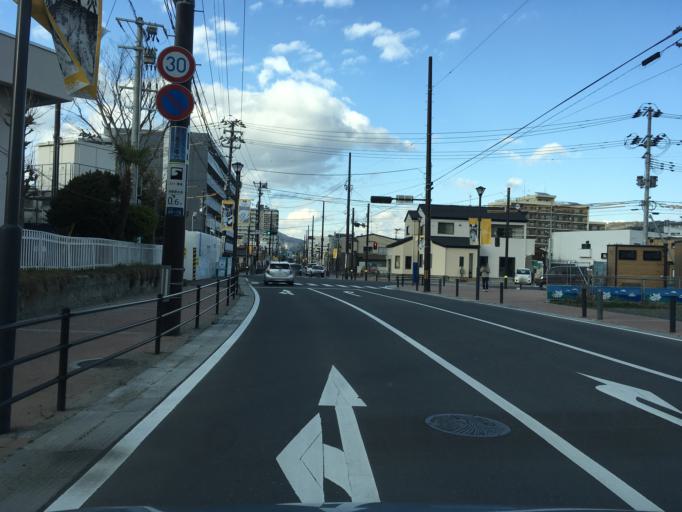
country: JP
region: Miyagi
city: Ishinomaki
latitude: 38.4283
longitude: 141.3057
